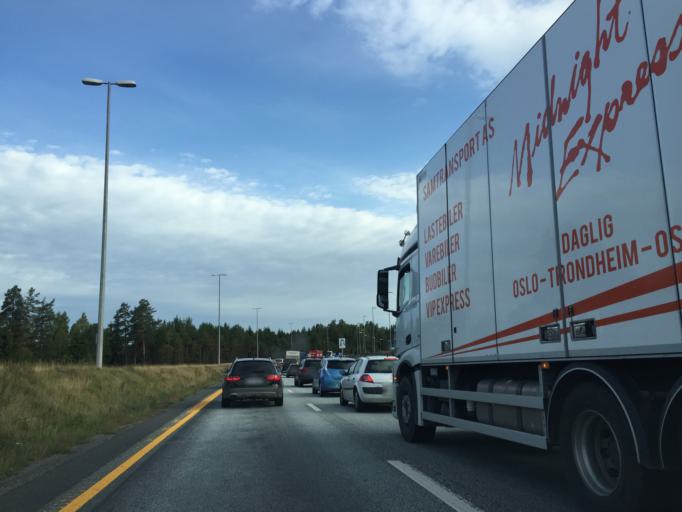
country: NO
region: Akershus
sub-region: Oppegard
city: Kolbotn
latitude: 59.8104
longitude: 10.8403
